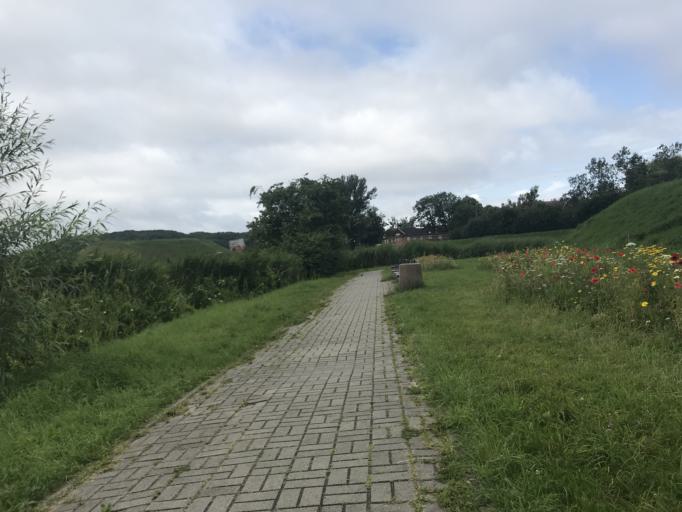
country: PL
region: Pomeranian Voivodeship
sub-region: Gdansk
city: Gdansk
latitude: 54.3379
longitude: 18.6534
